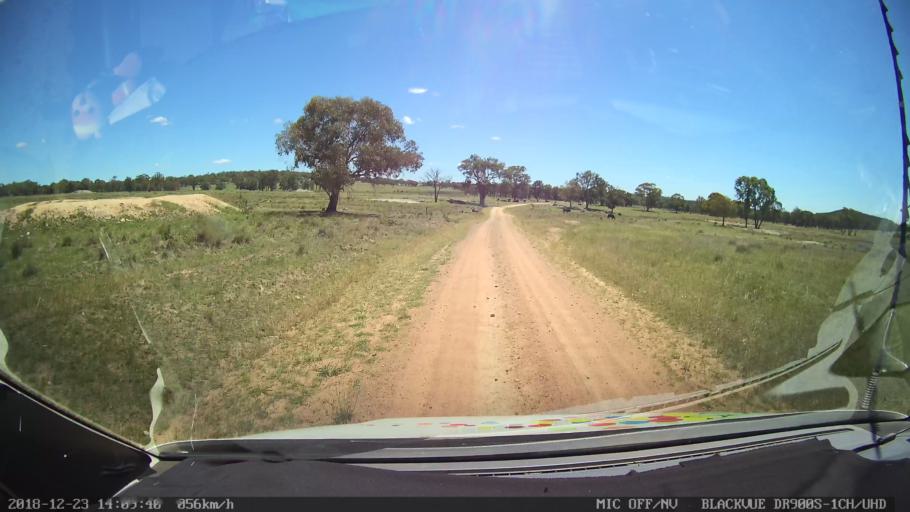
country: AU
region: New South Wales
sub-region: Tamworth Municipality
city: Manilla
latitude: -30.6465
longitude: 151.0607
